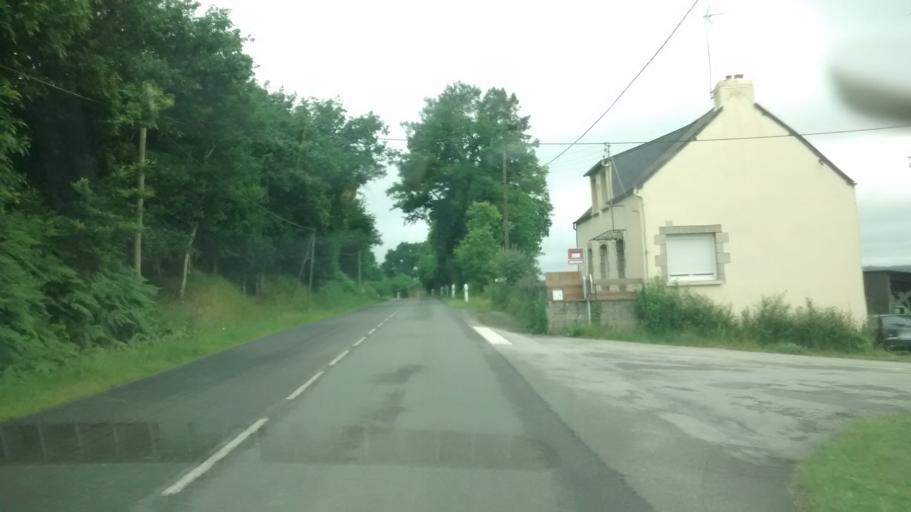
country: FR
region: Brittany
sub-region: Departement du Morbihan
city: Serent
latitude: 47.8188
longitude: -2.4717
